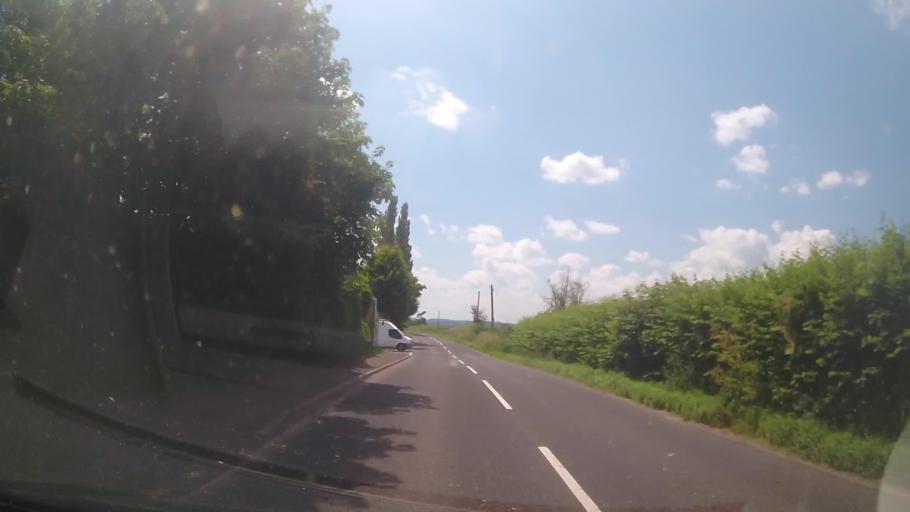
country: GB
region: England
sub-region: Herefordshire
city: Withington
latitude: 52.0508
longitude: -2.6206
